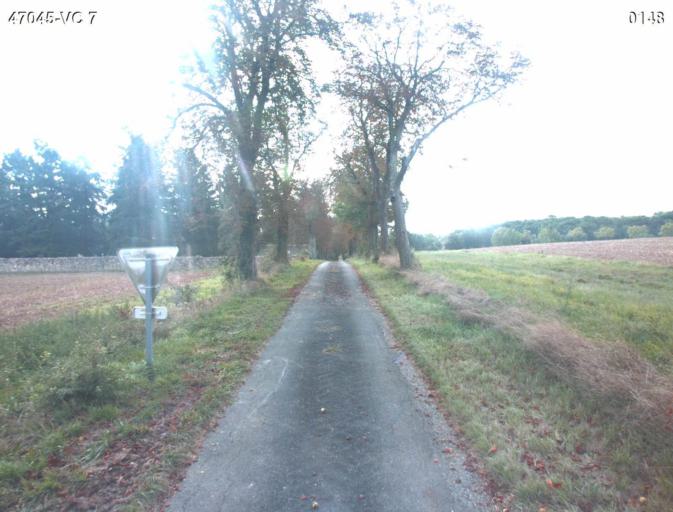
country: FR
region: Aquitaine
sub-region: Departement du Lot-et-Garonne
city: Nerac
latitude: 44.1388
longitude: 0.4316
